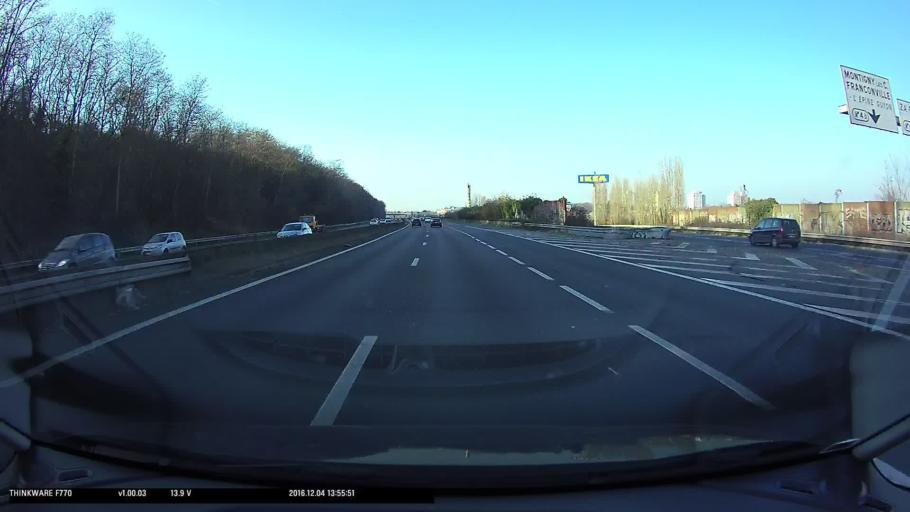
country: FR
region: Ile-de-France
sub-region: Departement du Val-d'Oise
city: Montigny-les-Cormeilles
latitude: 48.9856
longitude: 2.2134
